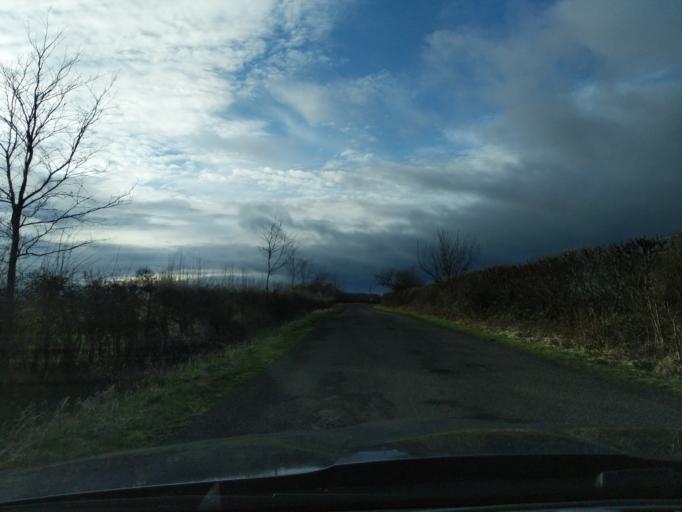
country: GB
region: England
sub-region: Northumberland
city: Ancroft
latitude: 55.6856
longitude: -1.9510
